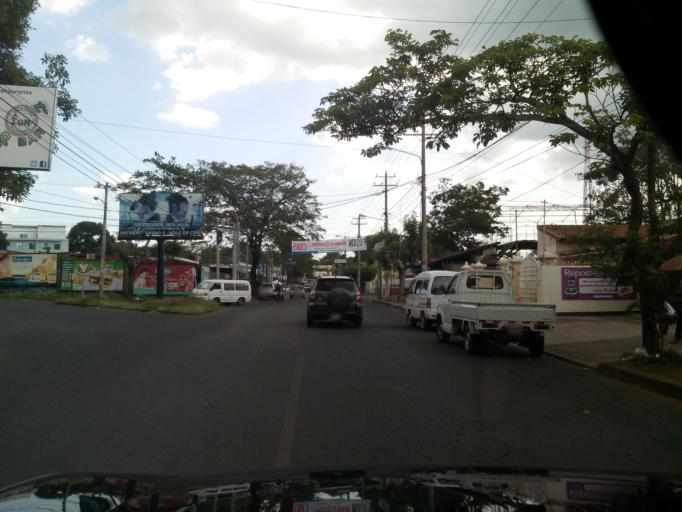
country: NI
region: Managua
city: Managua
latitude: 12.1218
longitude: -86.2604
